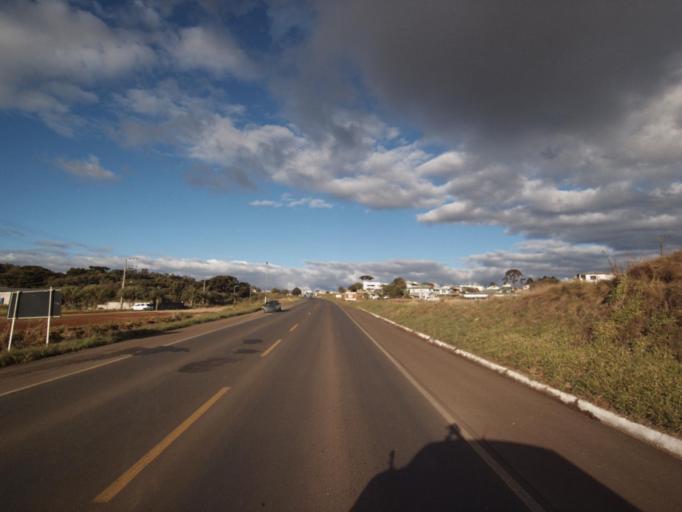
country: BR
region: Santa Catarina
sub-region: Campos Novos
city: Campos Novos
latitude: -27.3899
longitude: -51.2249
